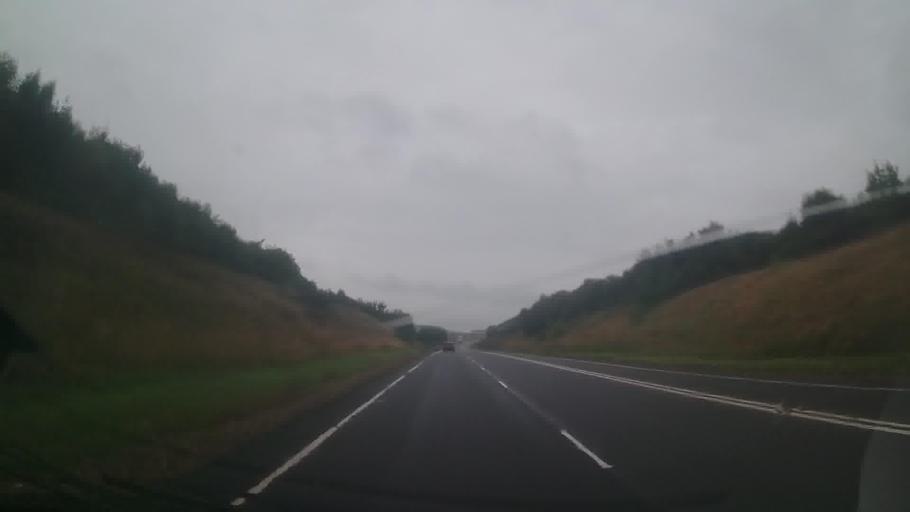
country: GB
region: Scotland
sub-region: North Ayrshire
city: Ardrossan
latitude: 55.6576
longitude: -4.8196
